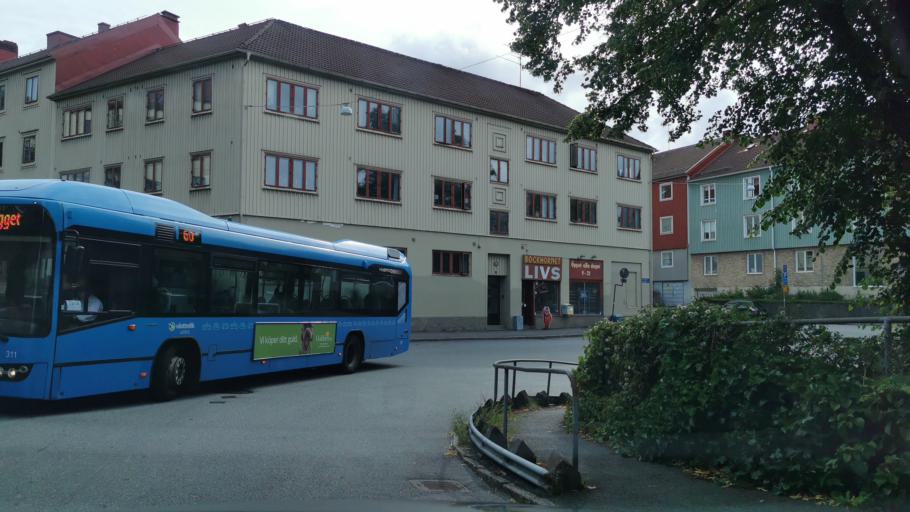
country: SE
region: Vaestra Goetaland
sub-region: Goteborg
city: Majorna
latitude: 57.6935
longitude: 11.9404
